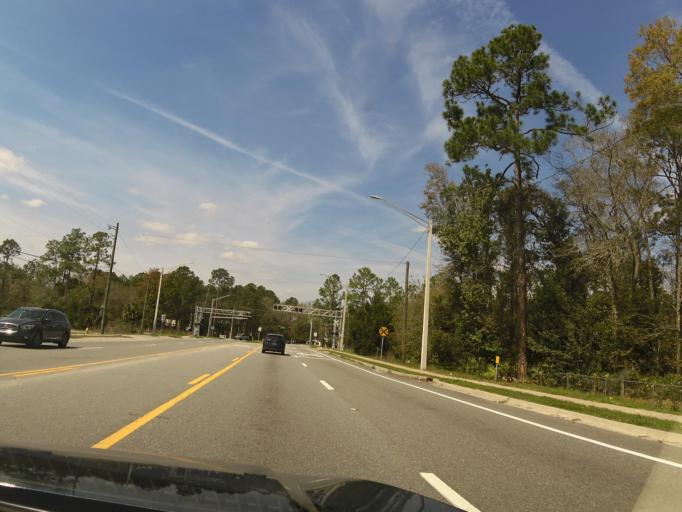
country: US
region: Florida
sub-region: Duval County
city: Jacksonville
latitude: 30.3190
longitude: -81.7925
